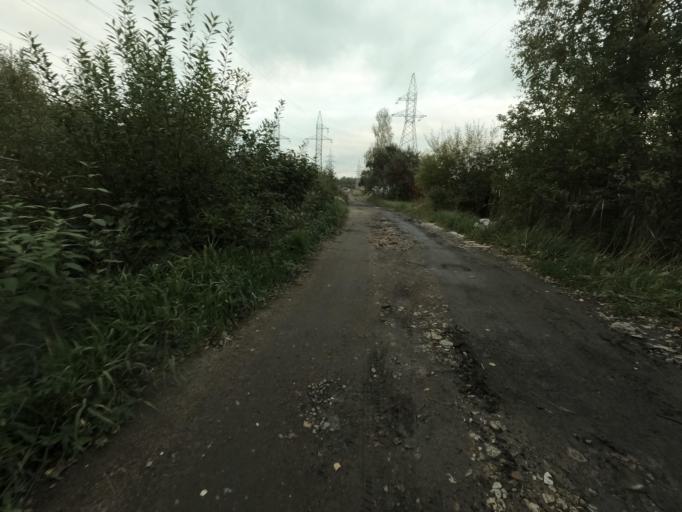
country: RU
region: St.-Petersburg
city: Sapernyy
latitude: 59.7740
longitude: 30.6514
